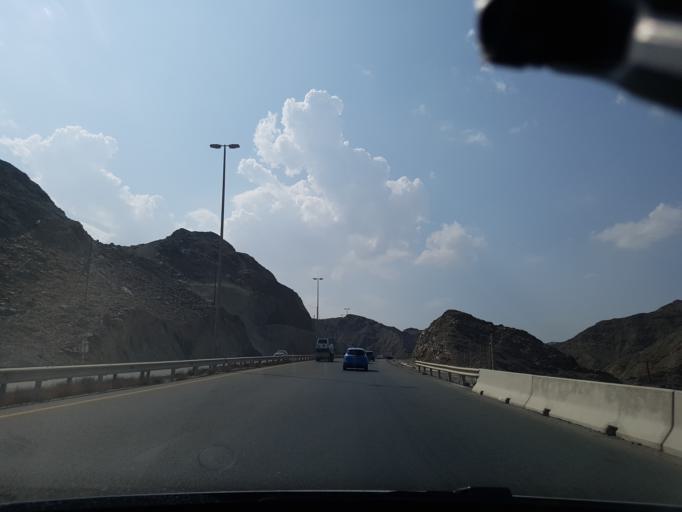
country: AE
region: Al Fujayrah
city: Dibba Al-Fujairah
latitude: 25.5299
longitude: 56.1460
